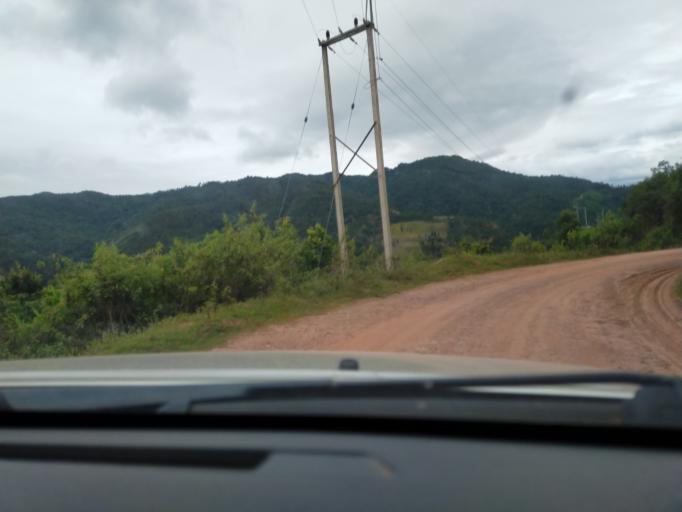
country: TH
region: Nan
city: Chaloem Phra Kiat
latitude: 19.7606
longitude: 101.3485
